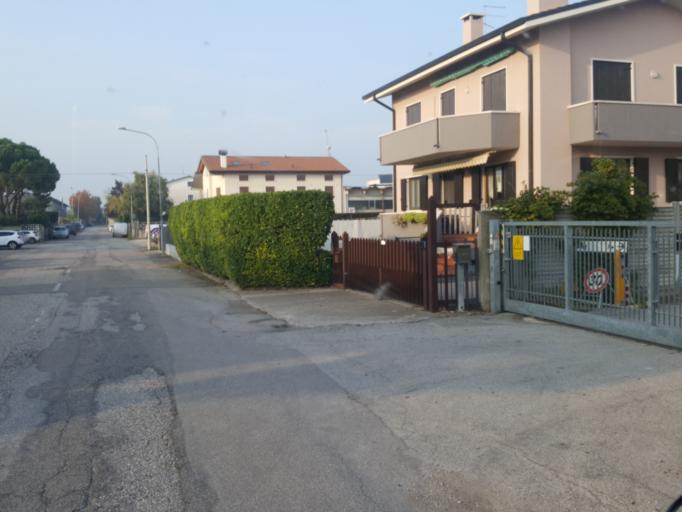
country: IT
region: Veneto
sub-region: Provincia di Verona
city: Zevio
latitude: 45.3687
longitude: 11.0951
